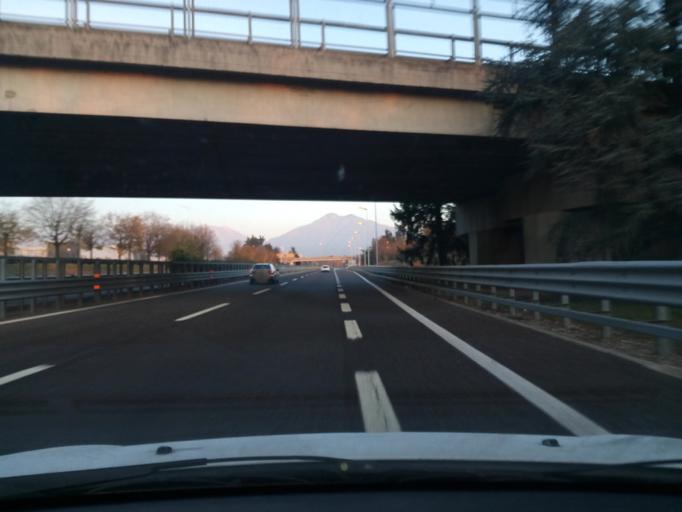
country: IT
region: Veneto
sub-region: Provincia di Vicenza
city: Thiene
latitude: 45.6795
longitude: 11.4638
